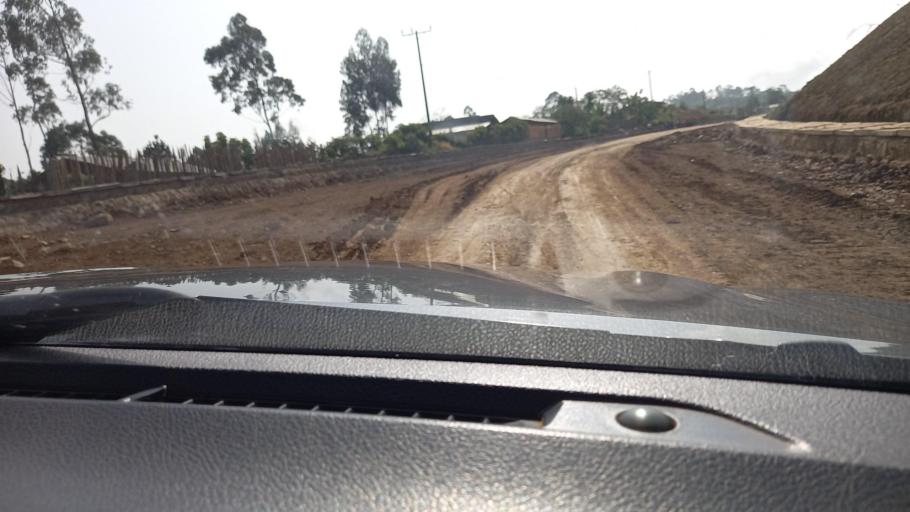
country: ET
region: Southern Nations, Nationalities, and People's Region
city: Mizan Teferi
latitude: 6.1654
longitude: 35.5901
